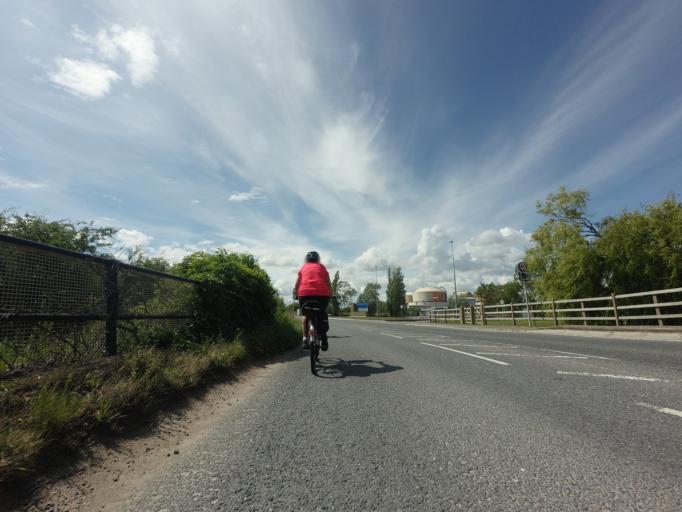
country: GB
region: England
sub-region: Medway
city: Allhallows
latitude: 51.4456
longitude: 0.6813
